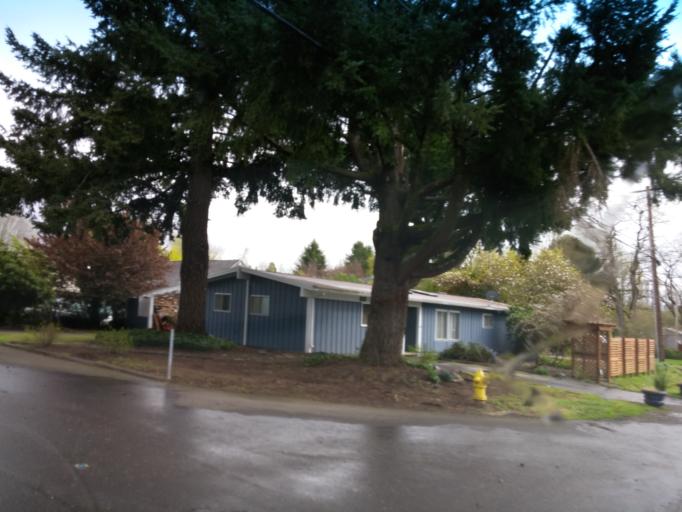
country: US
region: Oregon
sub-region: Washington County
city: Cedar Mill
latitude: 45.5157
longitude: -122.8274
